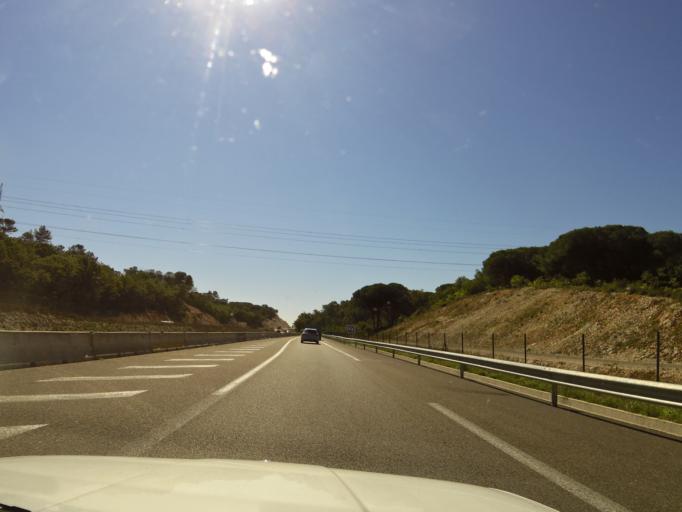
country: FR
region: Languedoc-Roussillon
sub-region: Departement du Gard
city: La Calmette
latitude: 43.9143
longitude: 4.2649
